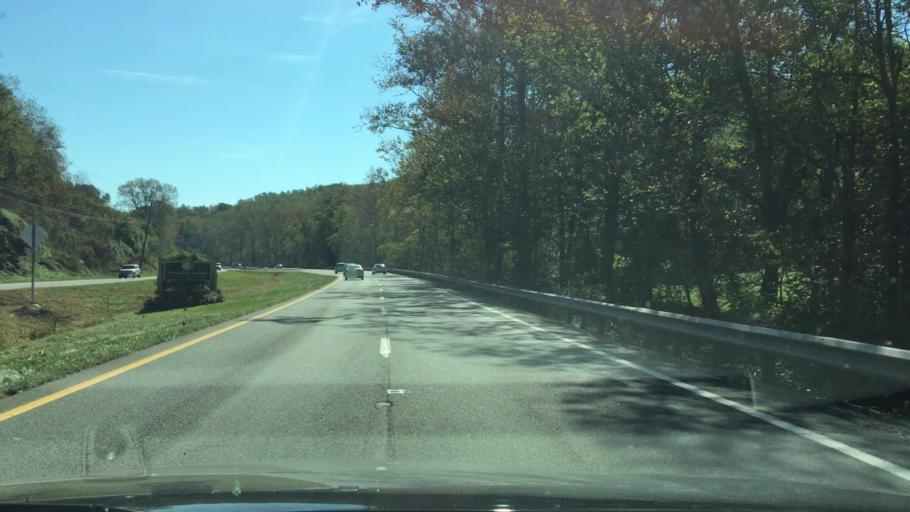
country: US
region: Virginia
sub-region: Roanoke County
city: Narrows
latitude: 37.1324
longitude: -79.9716
